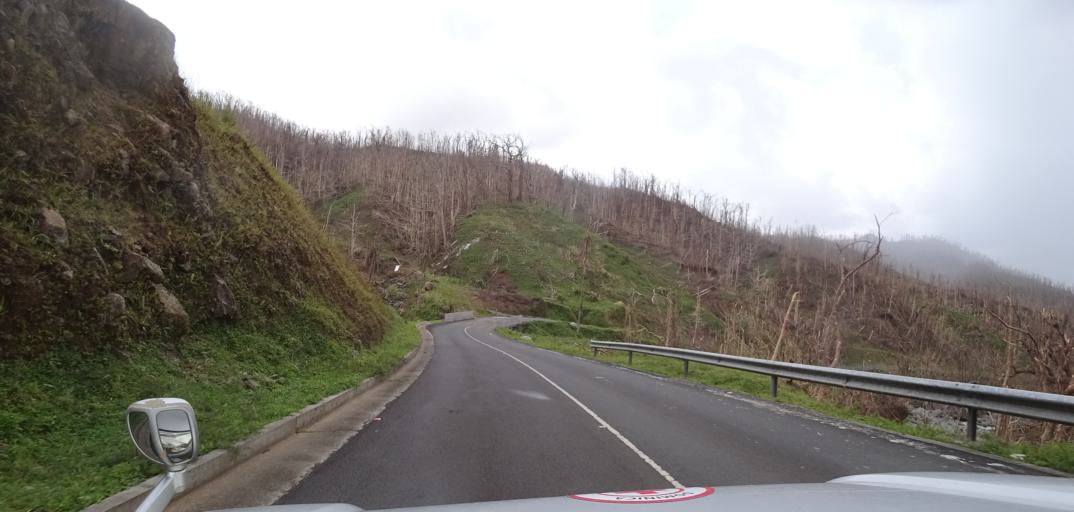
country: DM
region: Saint David
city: Castle Bruce
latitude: 15.4732
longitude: -61.3002
